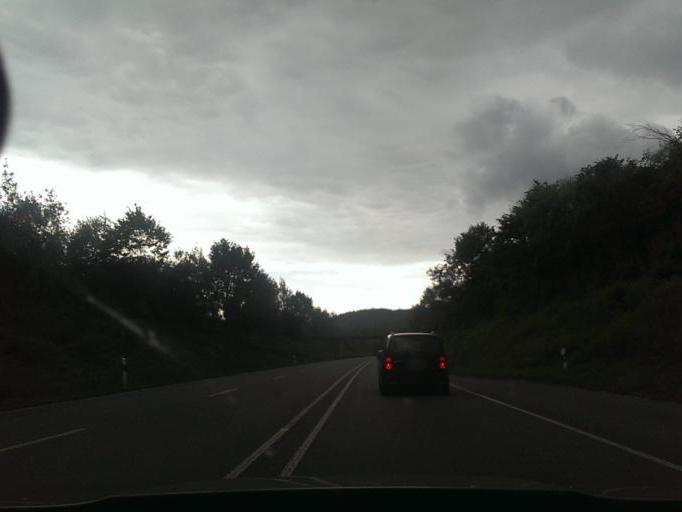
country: DE
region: North Rhine-Westphalia
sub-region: Regierungsbezirk Detmold
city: Horn
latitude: 51.8661
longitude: 8.9604
